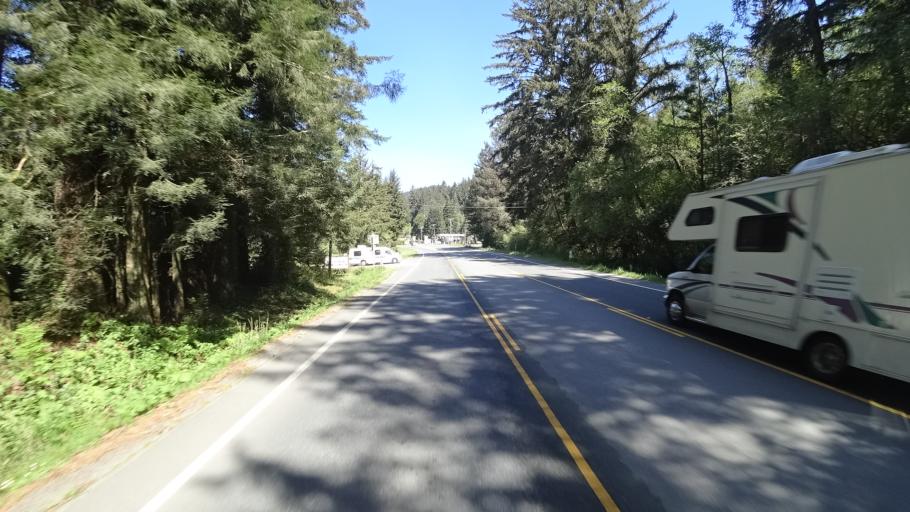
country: US
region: California
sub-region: Del Norte County
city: Bertsch-Oceanview
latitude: 41.5764
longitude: -124.0736
